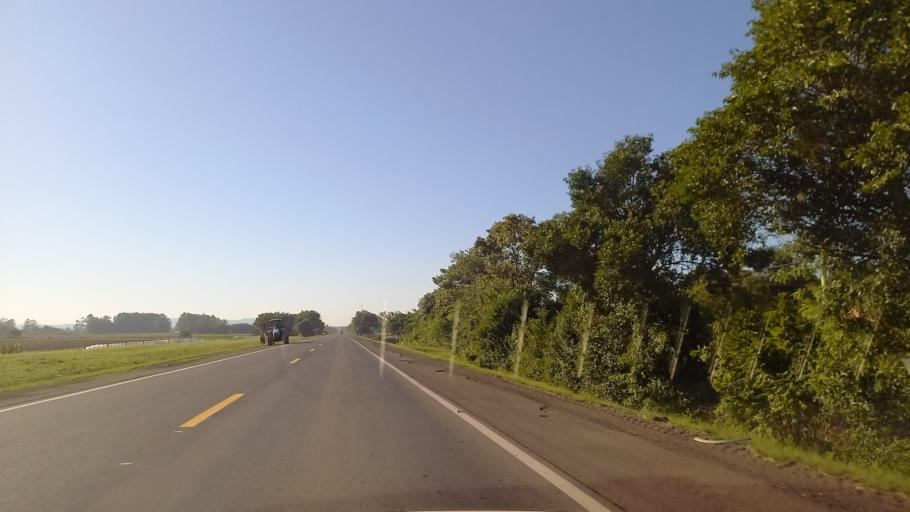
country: BR
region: Rio Grande do Sul
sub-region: Venancio Aires
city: Venancio Aires
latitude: -29.6613
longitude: -52.0684
